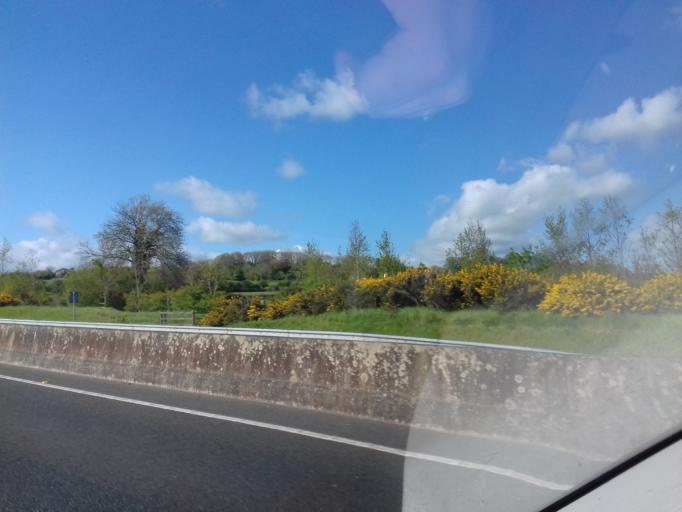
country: IE
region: Munster
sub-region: Waterford
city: Waterford
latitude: 52.3350
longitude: -7.1588
